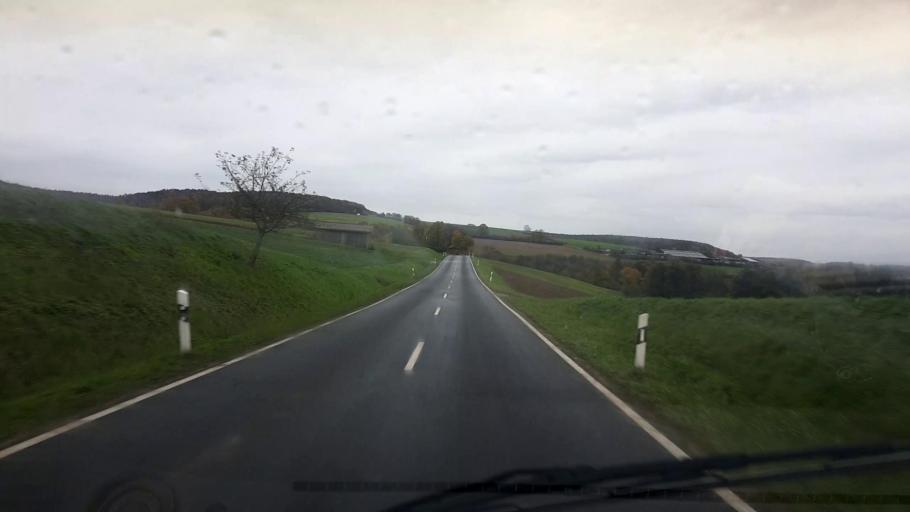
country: DE
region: Bavaria
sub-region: Upper Franconia
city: Burgwindheim
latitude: 49.8797
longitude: 10.5838
